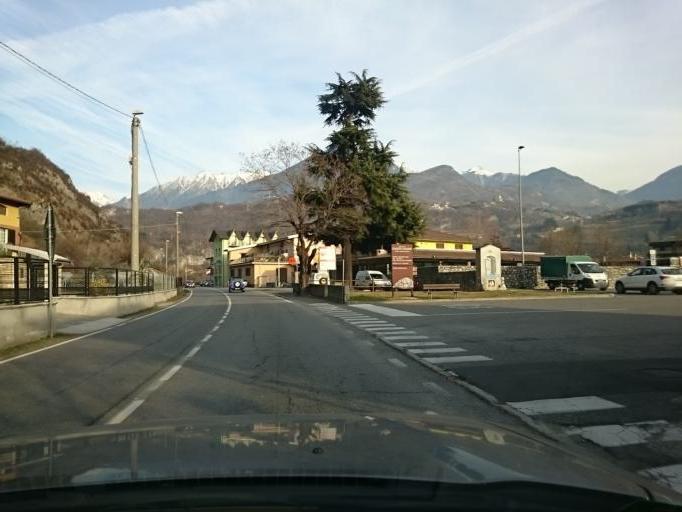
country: IT
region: Lombardy
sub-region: Provincia di Brescia
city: Cividate Camuno
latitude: 45.9432
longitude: 10.2703
